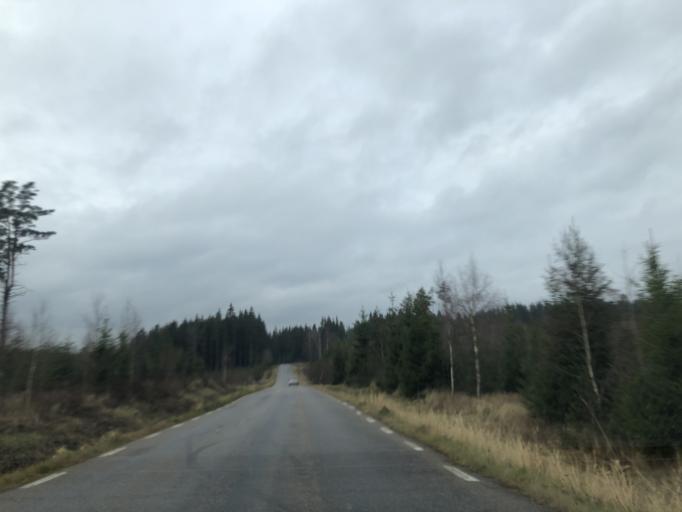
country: SE
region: Vaestra Goetaland
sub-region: Ulricehamns Kommun
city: Ulricehamn
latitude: 57.8949
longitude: 13.5025
